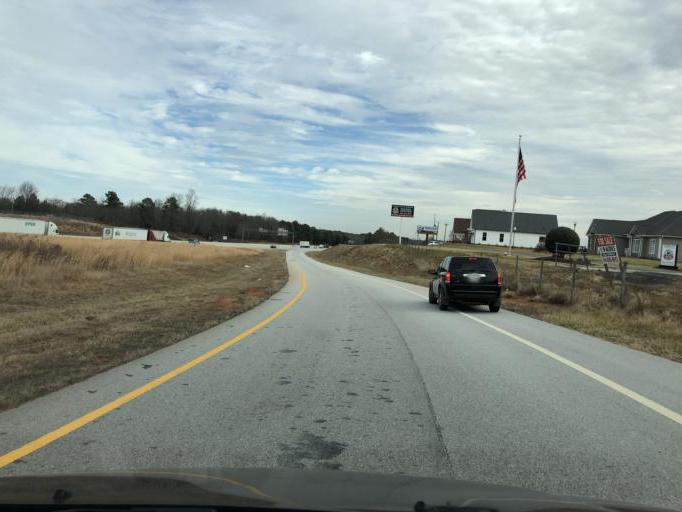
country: US
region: South Carolina
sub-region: Greenville County
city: Greer
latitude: 34.8857
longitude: -82.1885
